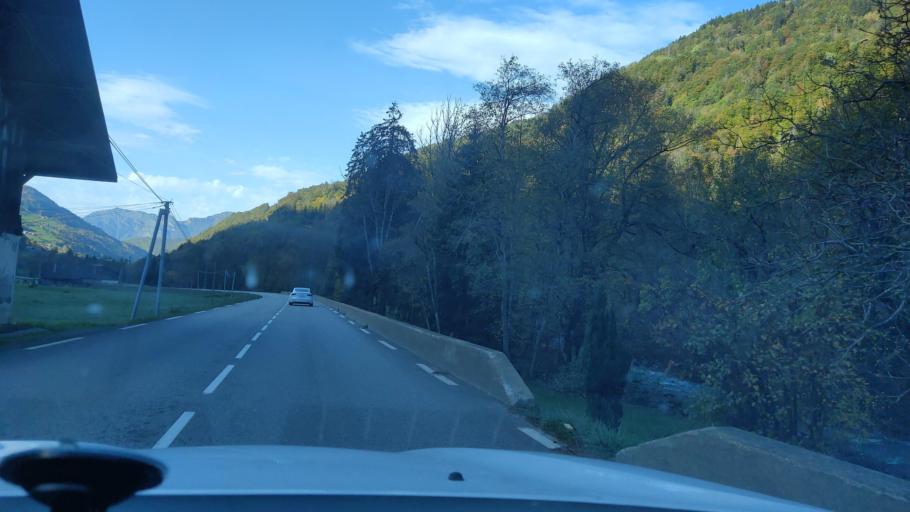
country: FR
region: Rhone-Alpes
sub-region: Departement de la Savoie
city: Beaufort
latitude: 45.7201
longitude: 6.5184
